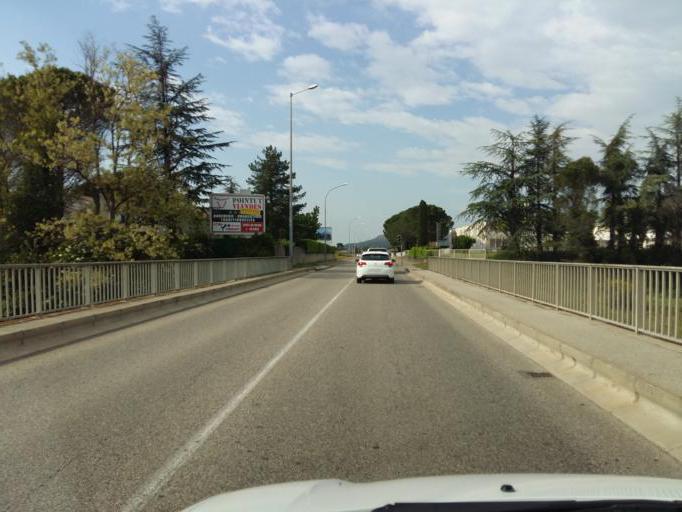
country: FR
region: Provence-Alpes-Cote d'Azur
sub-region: Departement du Vaucluse
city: Bollene
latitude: 44.2817
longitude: 4.7592
